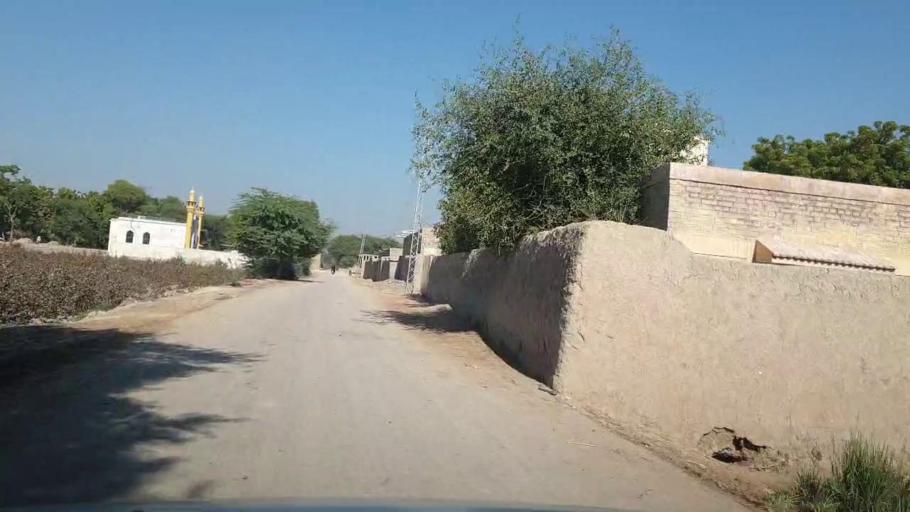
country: PK
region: Sindh
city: Johi
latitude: 26.6671
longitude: 67.7056
